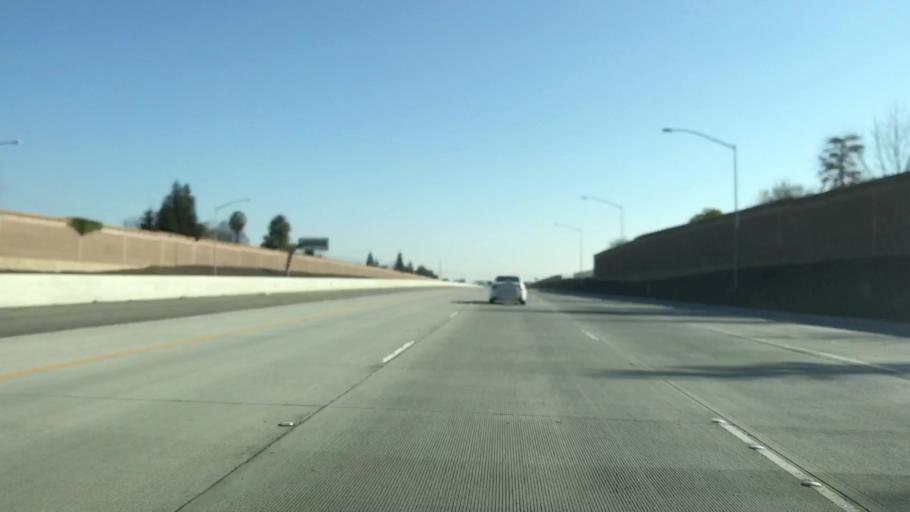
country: US
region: California
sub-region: Kern County
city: Greenacres
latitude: 35.3618
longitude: -119.1126
